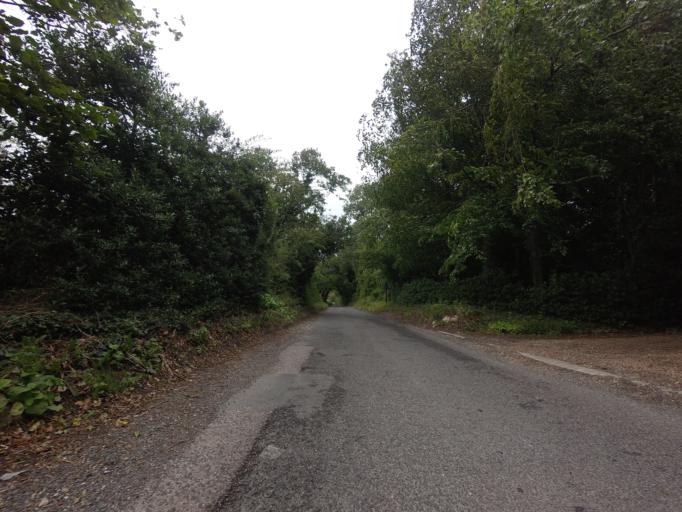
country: GB
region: England
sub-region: Kent
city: Borough Green
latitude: 51.3075
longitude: 0.2687
